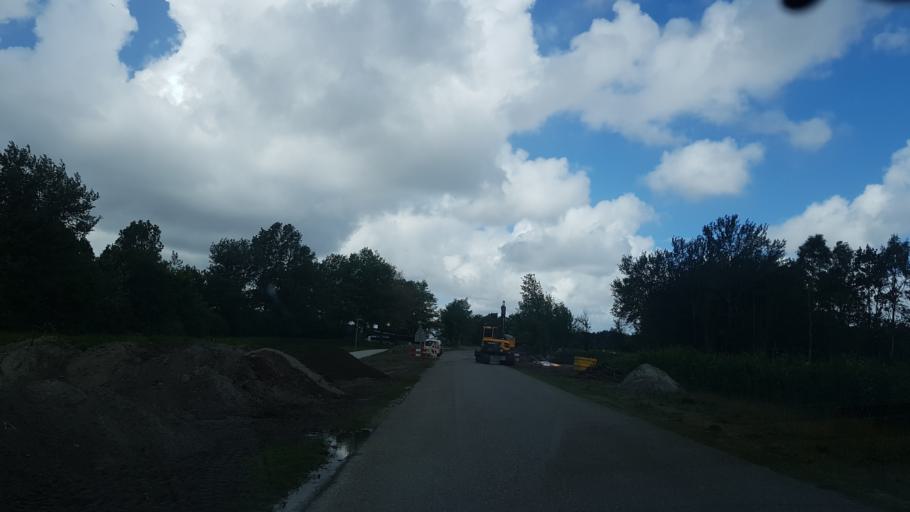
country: NL
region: Friesland
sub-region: Gemeente Dongeradeel
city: Anjum
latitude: 53.4031
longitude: 6.2155
